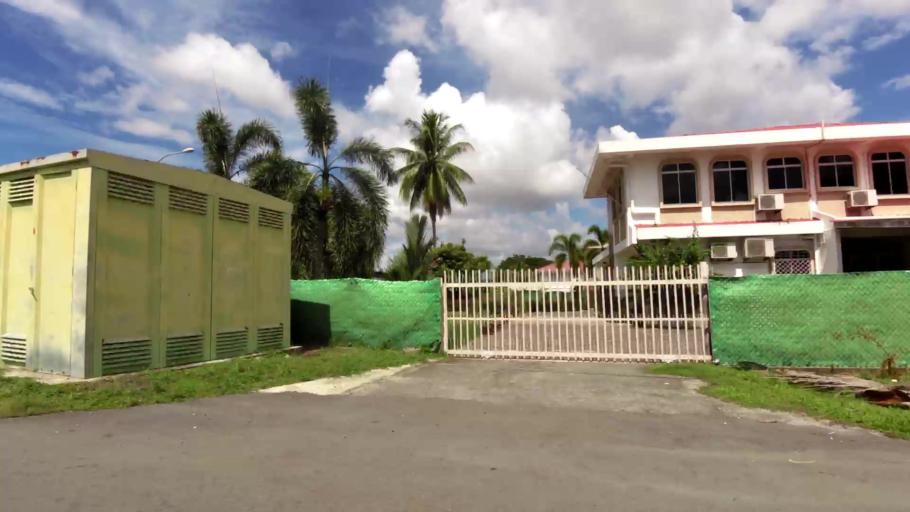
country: BN
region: Brunei and Muara
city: Bandar Seri Begawan
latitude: 4.9734
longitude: 114.9424
